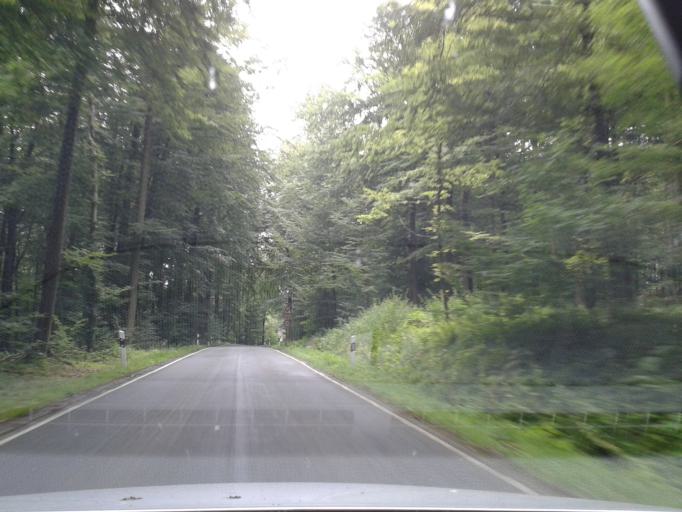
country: DE
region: North Rhine-Westphalia
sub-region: Regierungsbezirk Detmold
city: Barntrup
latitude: 51.9488
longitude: 9.1408
